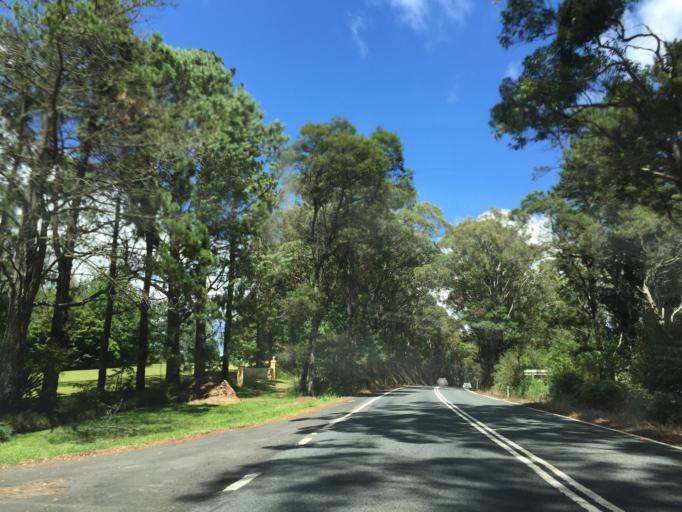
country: AU
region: New South Wales
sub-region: Blue Mountains Municipality
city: Lawson
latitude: -33.5184
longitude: 150.4659
